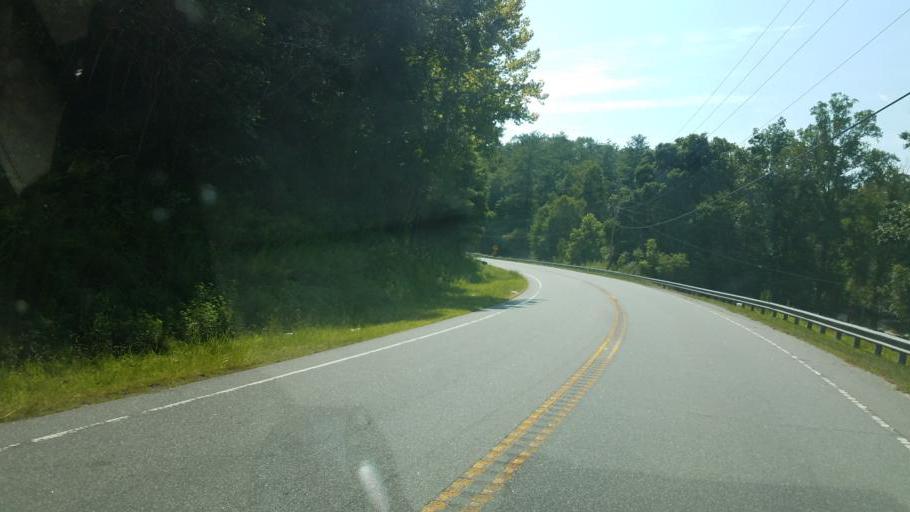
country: US
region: North Carolina
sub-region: Burke County
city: Glen Alpine
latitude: 35.8628
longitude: -81.7895
